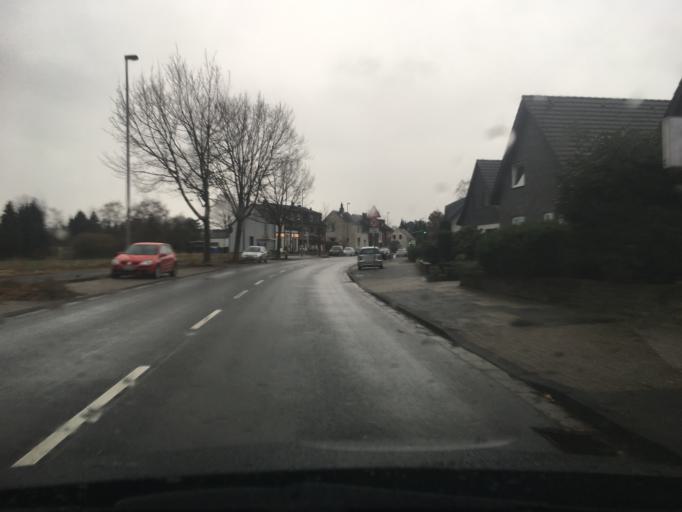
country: DE
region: North Rhine-Westphalia
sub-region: Regierungsbezirk Dusseldorf
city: Oberhausen
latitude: 51.5565
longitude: 6.8394
